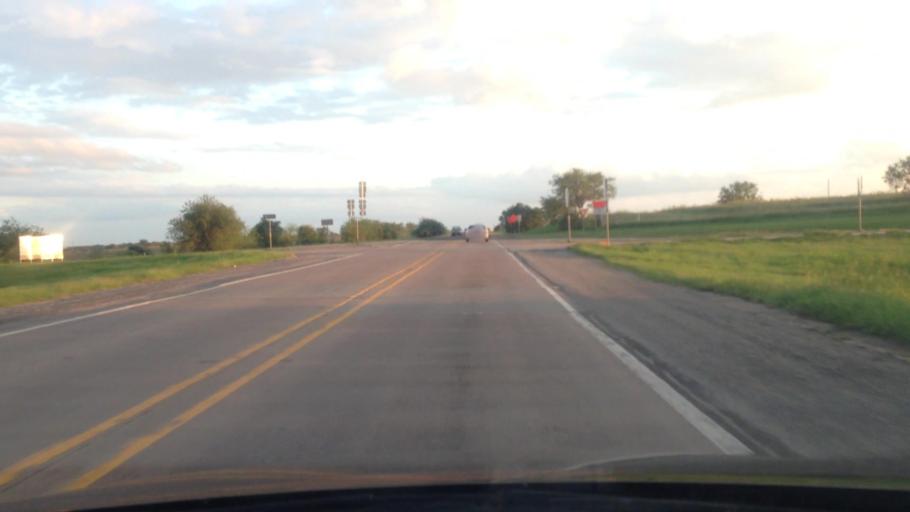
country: US
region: Texas
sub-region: Tarrant County
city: Benbrook
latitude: 32.6925
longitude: -97.4991
